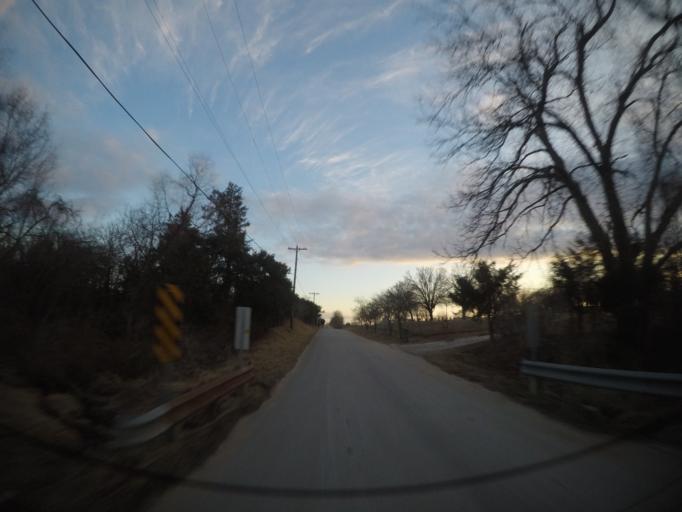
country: US
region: Kansas
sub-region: Wyandotte County
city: Bonner Springs
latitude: 39.0506
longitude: -94.9088
